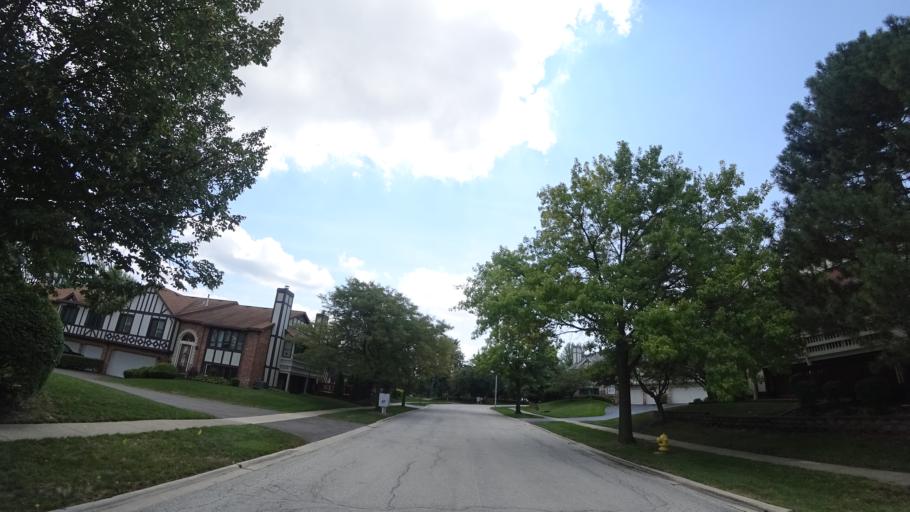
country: US
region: Illinois
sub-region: Cook County
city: Orland Hills
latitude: 41.5709
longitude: -87.8425
